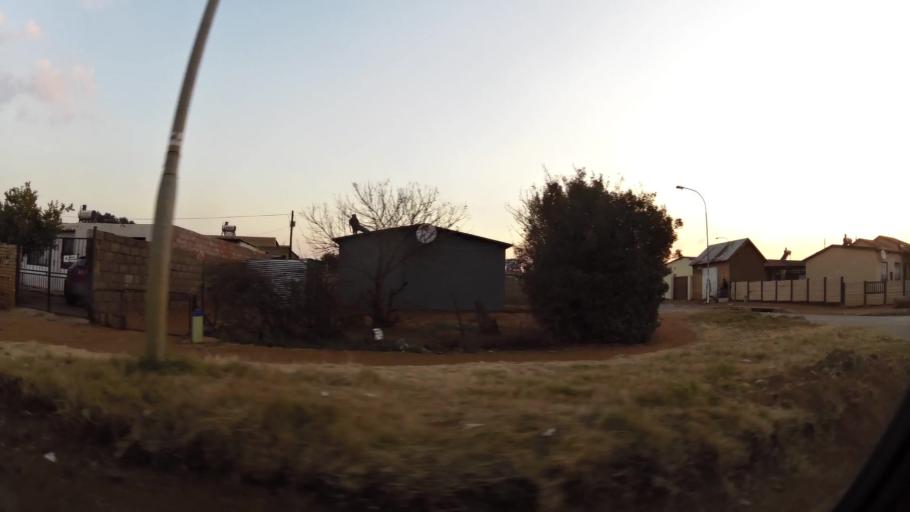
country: ZA
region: Gauteng
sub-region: City of Johannesburg Metropolitan Municipality
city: Soweto
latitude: -26.2844
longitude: 27.8805
